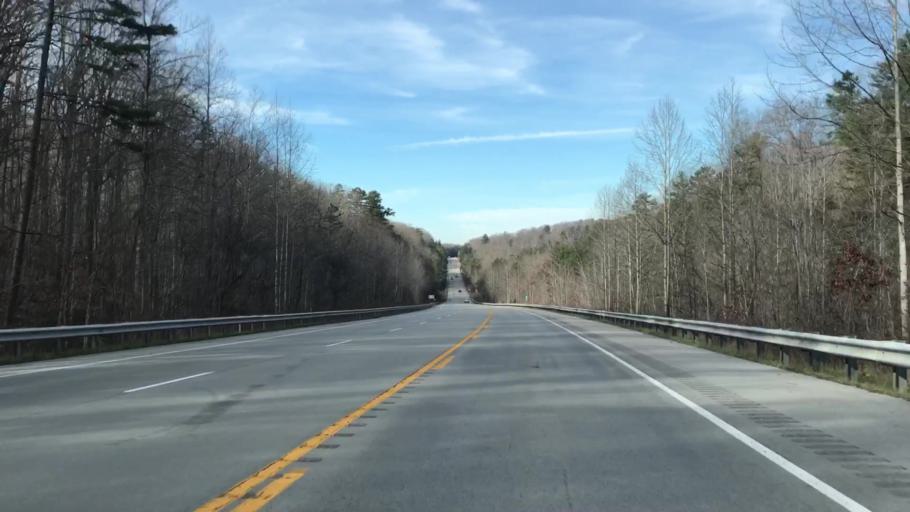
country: US
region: Kentucky
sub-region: McCreary County
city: Whitley City
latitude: 36.9012
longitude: -84.4990
